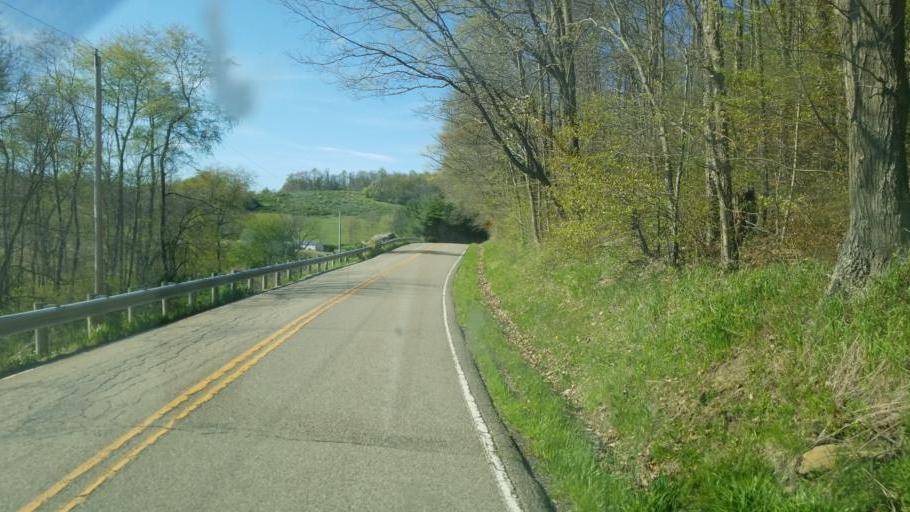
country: US
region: Ohio
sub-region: Coshocton County
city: Coshocton
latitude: 40.3624
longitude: -81.9600
